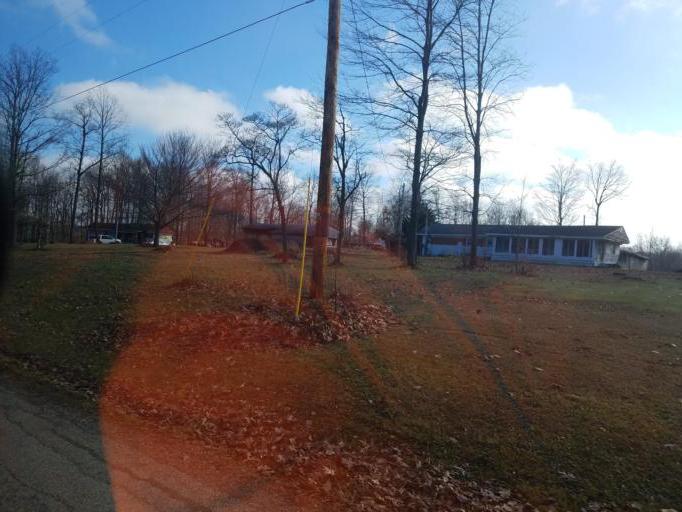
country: US
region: Ohio
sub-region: Sandusky County
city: Bellville
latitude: 40.5828
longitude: -82.5400
